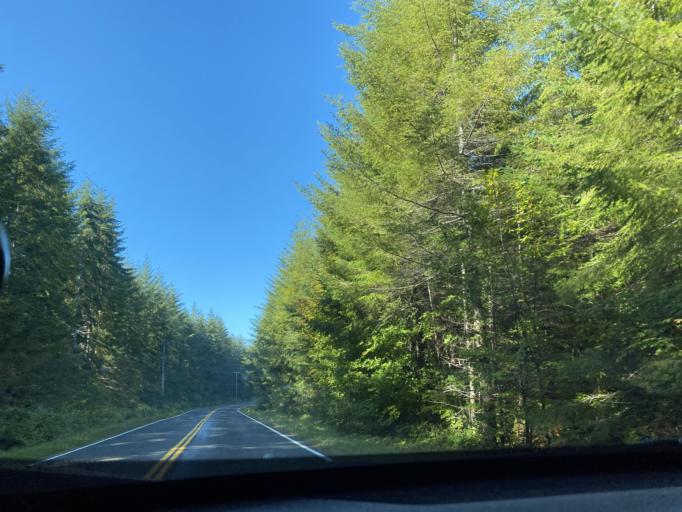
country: US
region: Washington
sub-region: Clallam County
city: Forks
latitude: 47.9472
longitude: -124.4843
